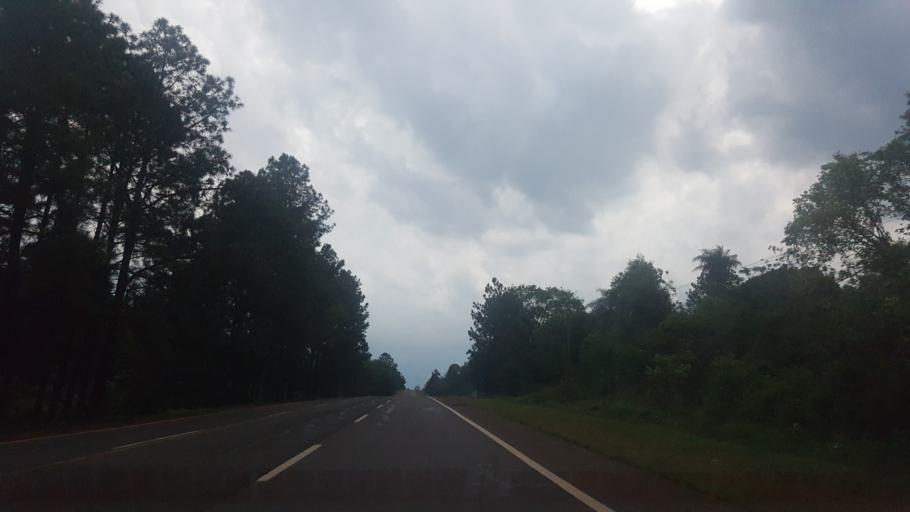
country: AR
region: Misiones
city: Santo Pipo
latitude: -27.1226
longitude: -55.3771
